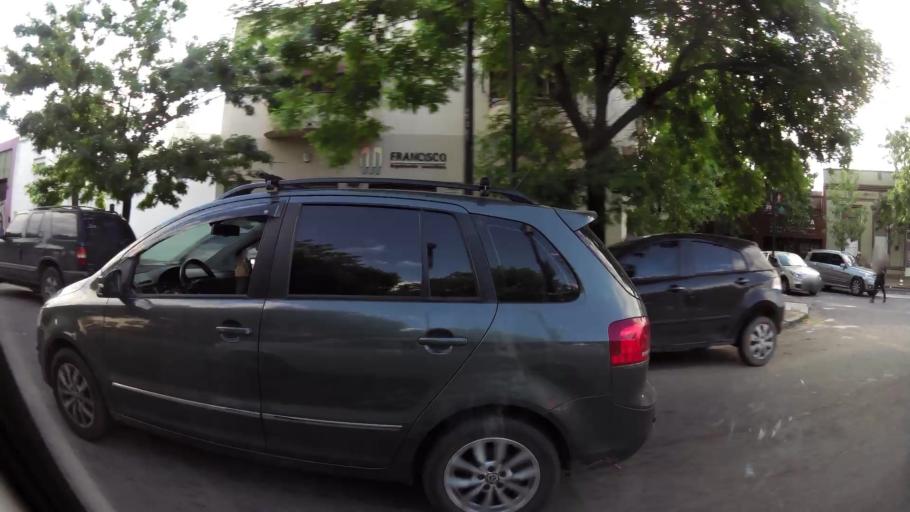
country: AR
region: Buenos Aires
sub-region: Partido de La Plata
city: La Plata
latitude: -34.9022
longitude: -57.9558
